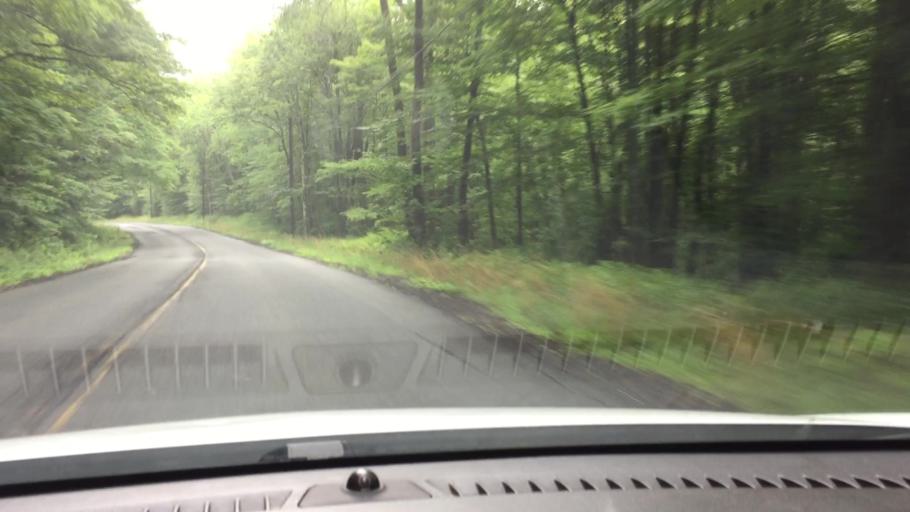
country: US
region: Massachusetts
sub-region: Berkshire County
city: Dalton
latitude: 42.4578
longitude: -73.1632
